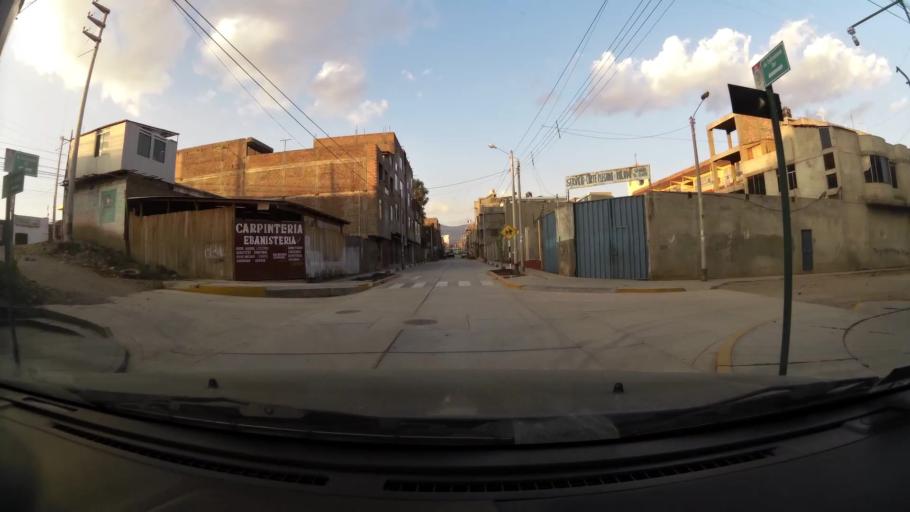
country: PE
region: Junin
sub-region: Provincia de Huancayo
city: Pilcomay
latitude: -12.0453
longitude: -75.2282
